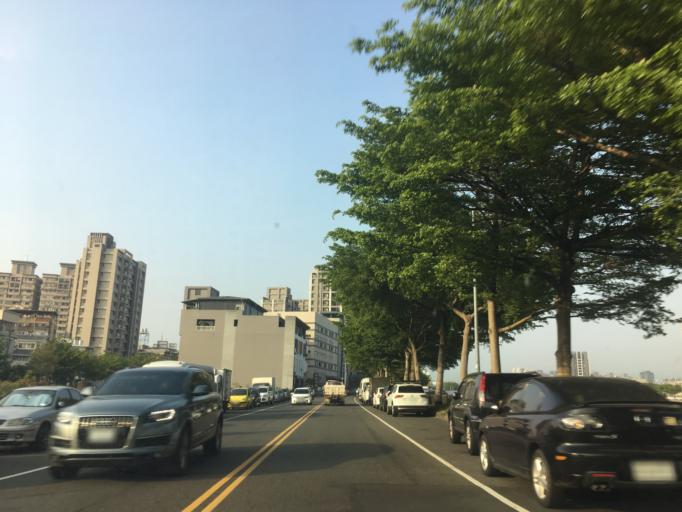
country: TW
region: Taiwan
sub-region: Taichung City
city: Taichung
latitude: 24.1506
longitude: 120.6999
